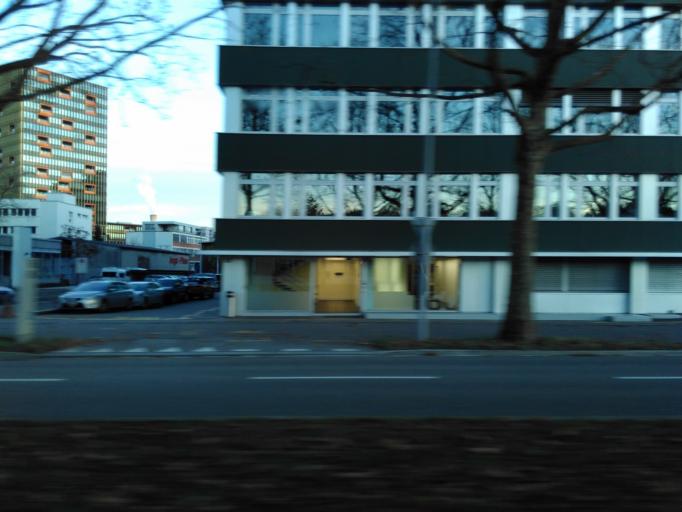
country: CH
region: Zurich
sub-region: Bezirk Zuerich
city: Zuerich (Kreis 11) / Seebach
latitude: 47.4167
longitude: 8.5533
